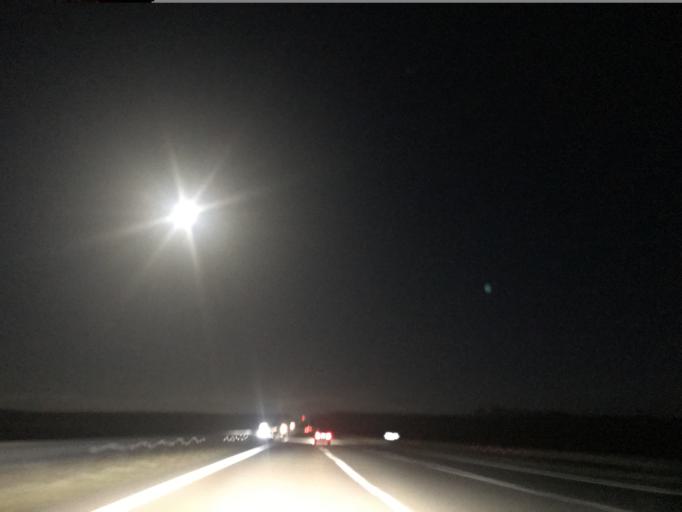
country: TR
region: Nigde
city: Ulukisla
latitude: 37.6398
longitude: 34.3868
